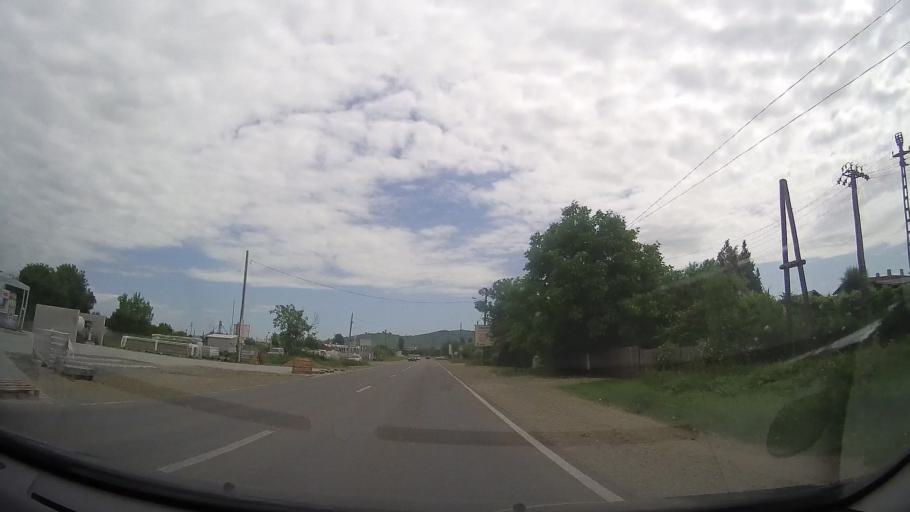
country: RO
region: Prahova
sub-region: Comuna Blejoiu
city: Blejoi
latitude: 45.0167
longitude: 26.0158
